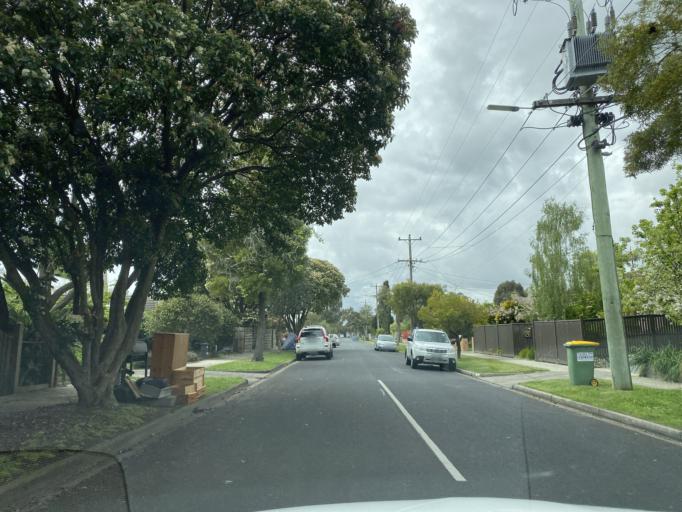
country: AU
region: Victoria
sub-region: Whitehorse
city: Burwood
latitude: -37.8432
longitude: 145.1257
